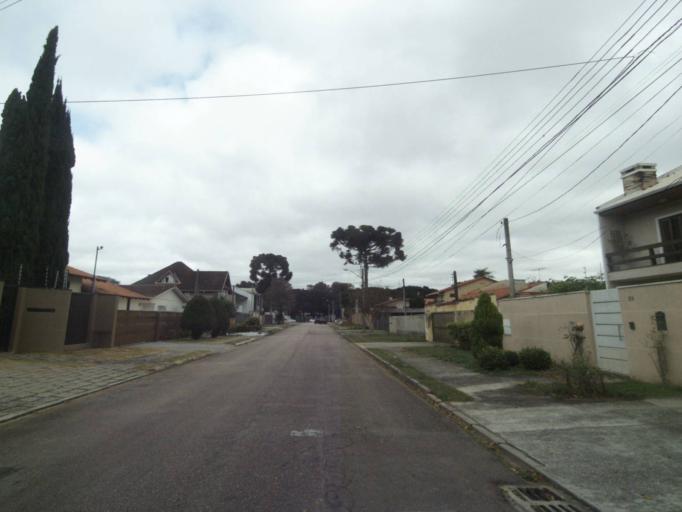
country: BR
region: Parana
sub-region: Curitiba
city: Curitiba
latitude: -25.4555
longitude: -49.3018
